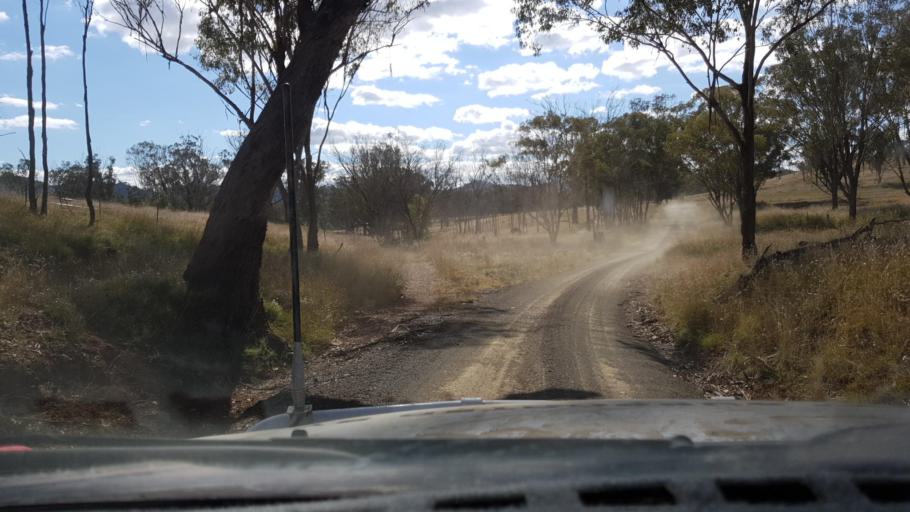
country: AU
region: New South Wales
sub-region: Tamworth Municipality
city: Manilla
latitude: -30.4666
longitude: 150.7776
